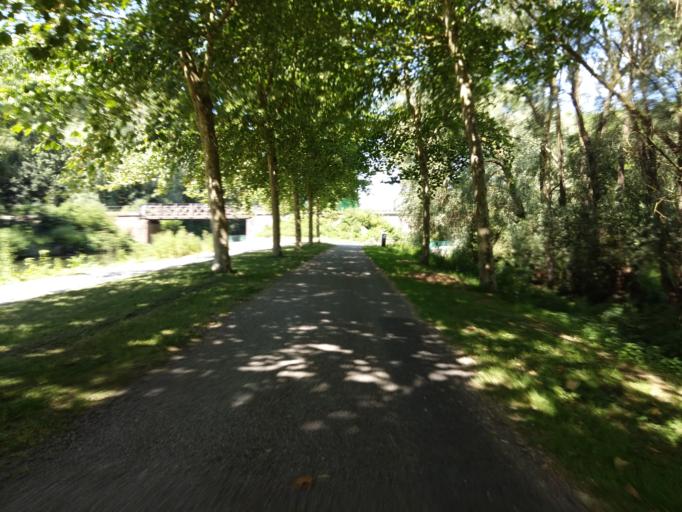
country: FR
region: Picardie
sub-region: Departement de la Somme
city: Amiens
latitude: 49.9159
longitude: 2.2671
